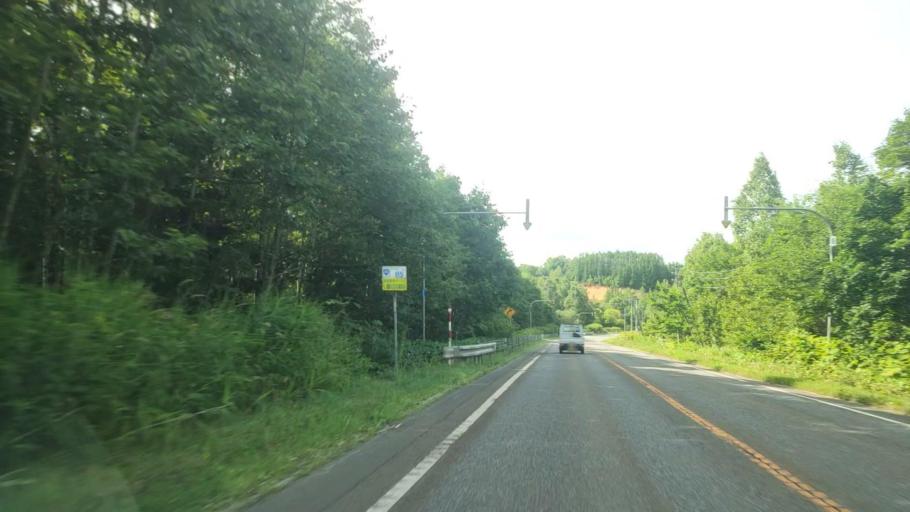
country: JP
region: Hokkaido
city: Nayoro
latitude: 44.3921
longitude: 142.3957
